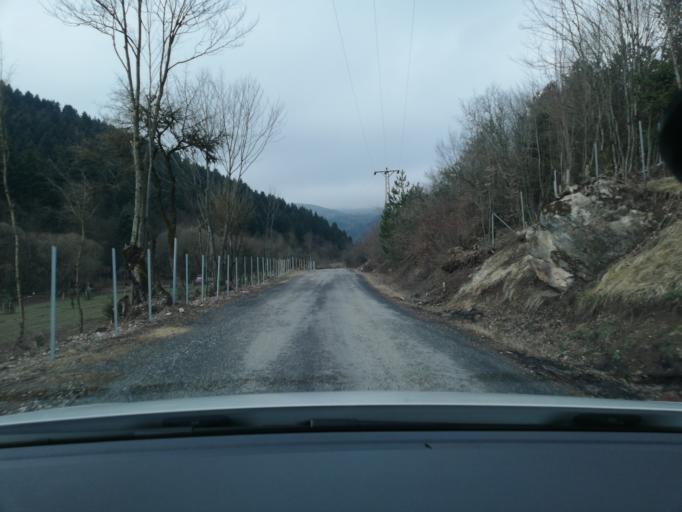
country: TR
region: Bolu
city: Bolu
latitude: 40.6850
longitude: 31.4639
